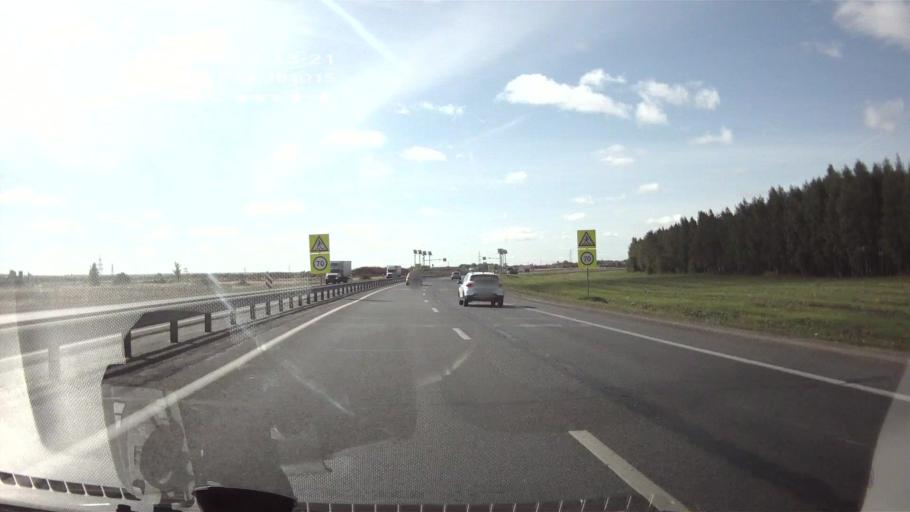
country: RU
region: Ulyanovsk
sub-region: Ulyanovskiy Rayon
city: Ulyanovsk
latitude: 54.2719
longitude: 48.2609
